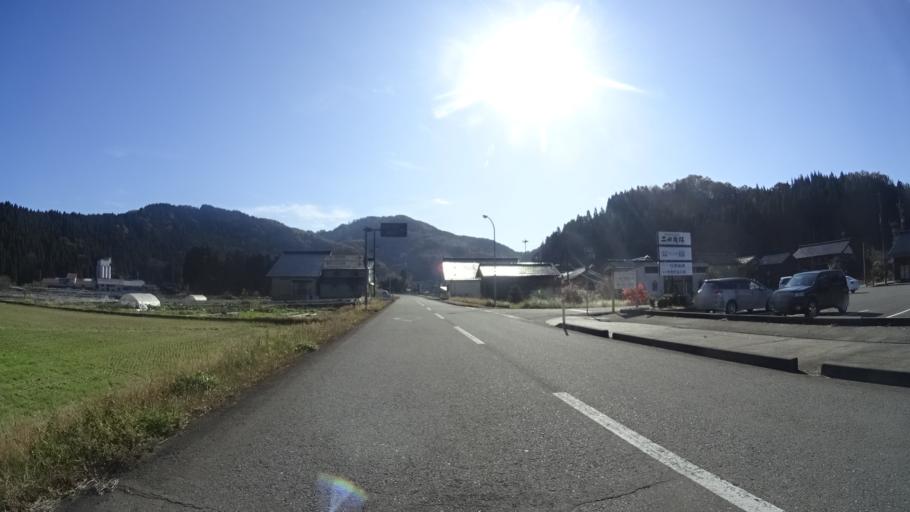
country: JP
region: Ishikawa
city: Tsurugi-asahimachi
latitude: 36.3604
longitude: 136.5998
